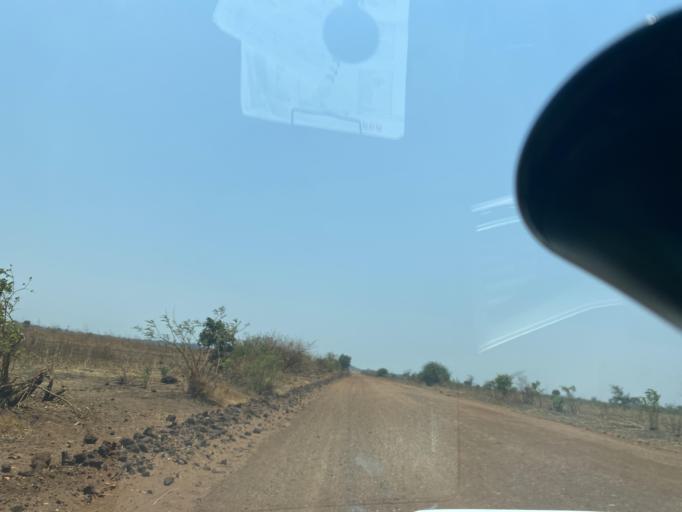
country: ZM
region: Lusaka
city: Lusaka
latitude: -15.4647
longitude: 27.9094
